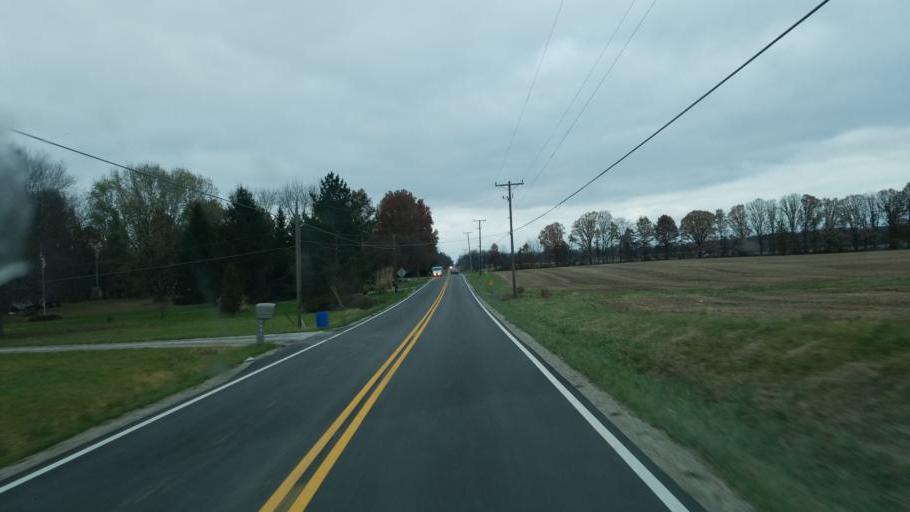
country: US
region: Ohio
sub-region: Delaware County
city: Sunbury
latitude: 40.2860
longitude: -82.9078
